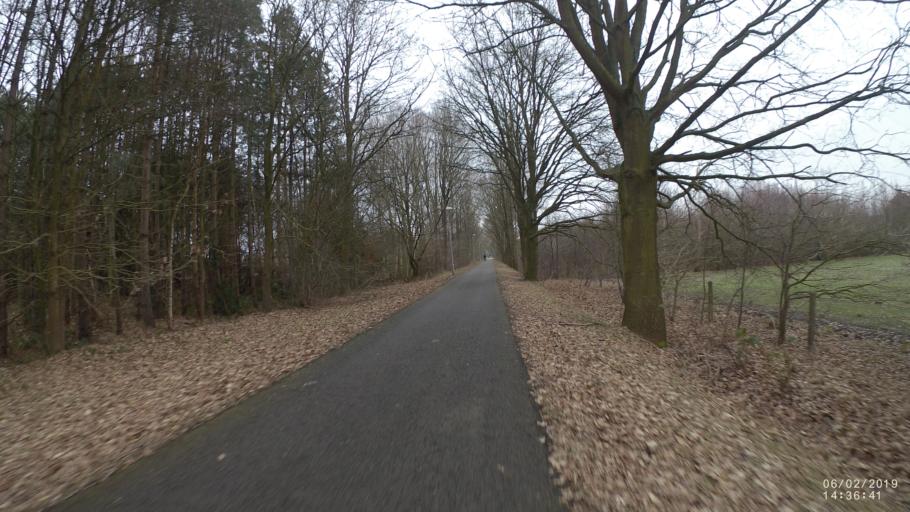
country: BE
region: Flanders
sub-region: Provincie Vlaams-Brabant
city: Aarschot
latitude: 51.0183
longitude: 4.8301
